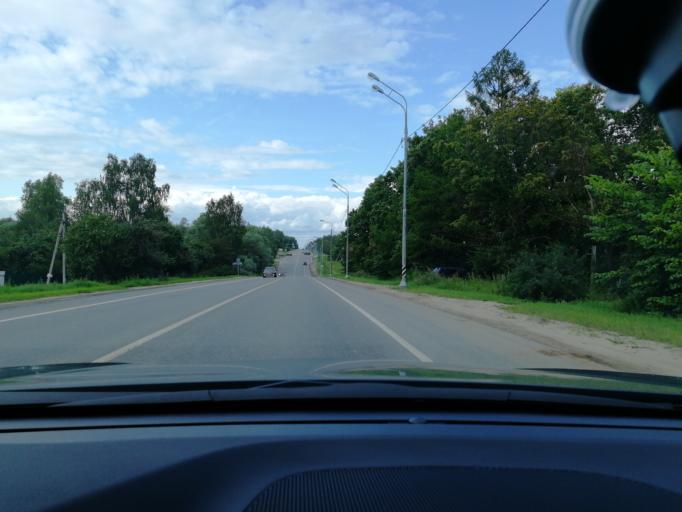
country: RU
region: Moskovskaya
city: Proletarskiy
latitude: 55.0378
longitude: 37.4298
